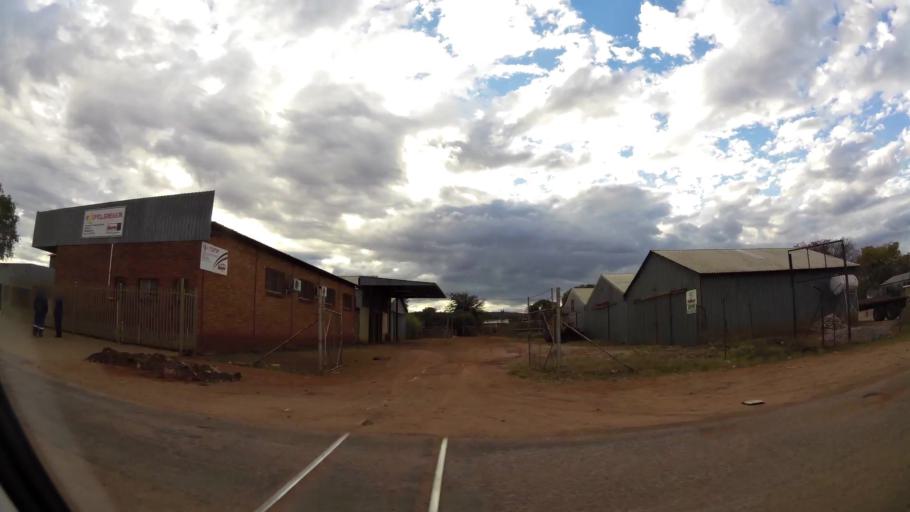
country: ZA
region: Limpopo
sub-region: Waterberg District Municipality
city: Modimolle
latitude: -24.5256
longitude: 28.7115
